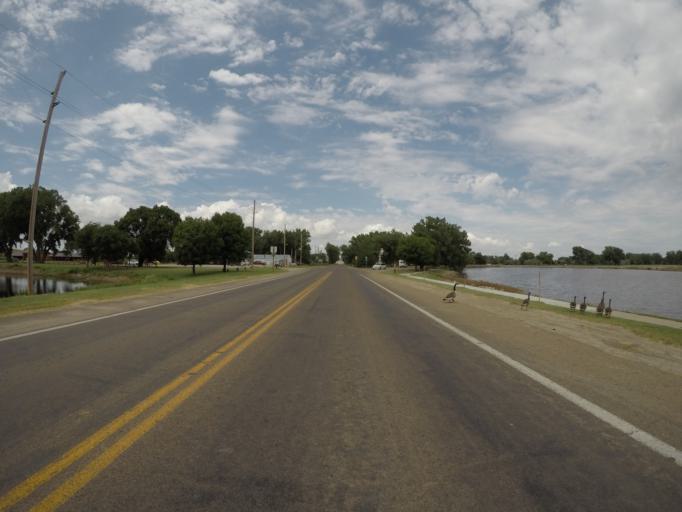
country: US
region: Kansas
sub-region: Rawlins County
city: Atwood
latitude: 39.8153
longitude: -101.0468
